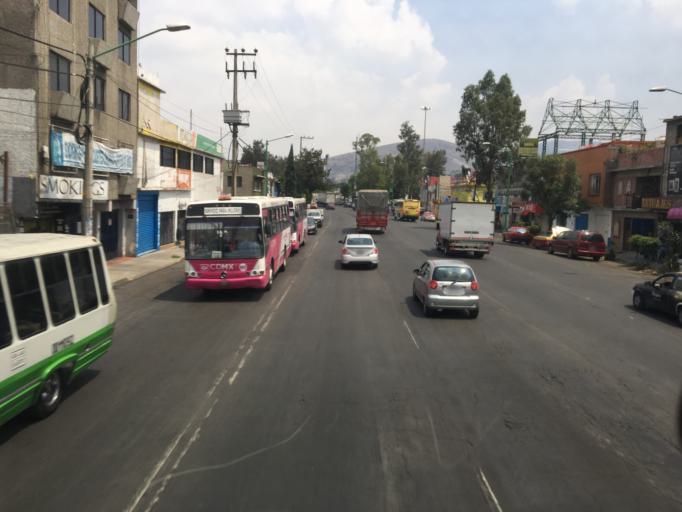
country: MX
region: Mexico
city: Tlalnepantla
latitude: 19.5204
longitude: -99.1571
